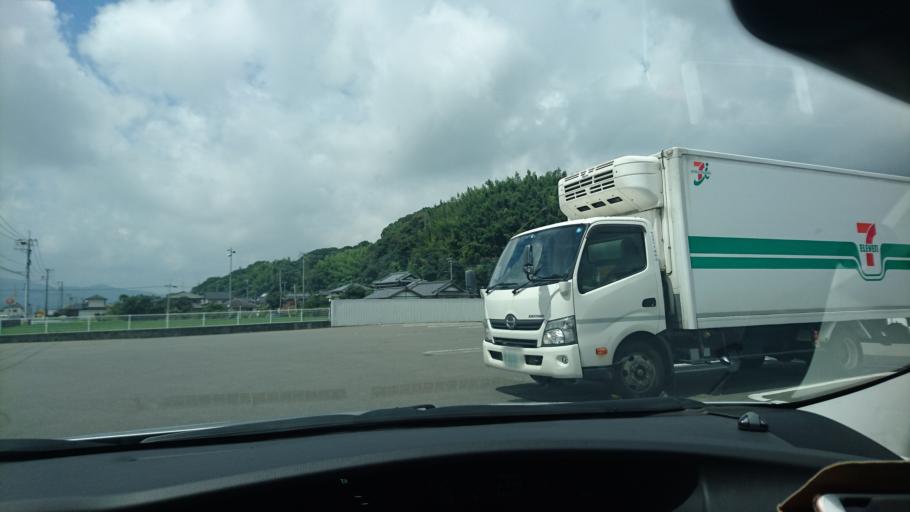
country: JP
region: Saga Prefecture
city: Takeocho-takeo
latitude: 33.2163
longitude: 130.1331
